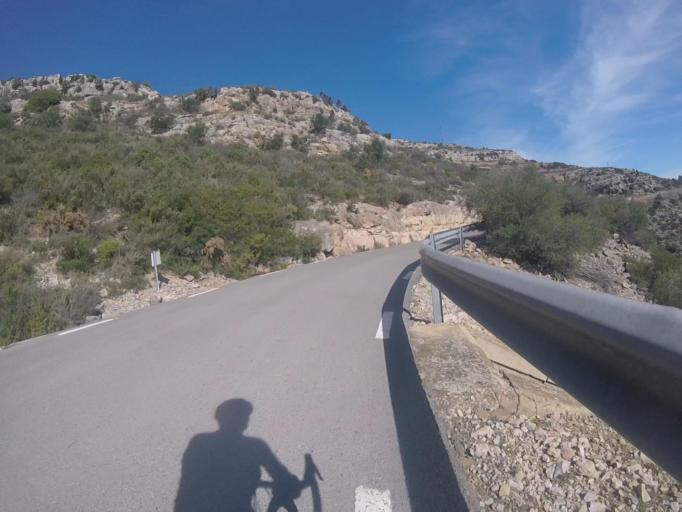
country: ES
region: Valencia
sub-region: Provincia de Castello
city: Sarratella
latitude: 40.2830
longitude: 0.0366
